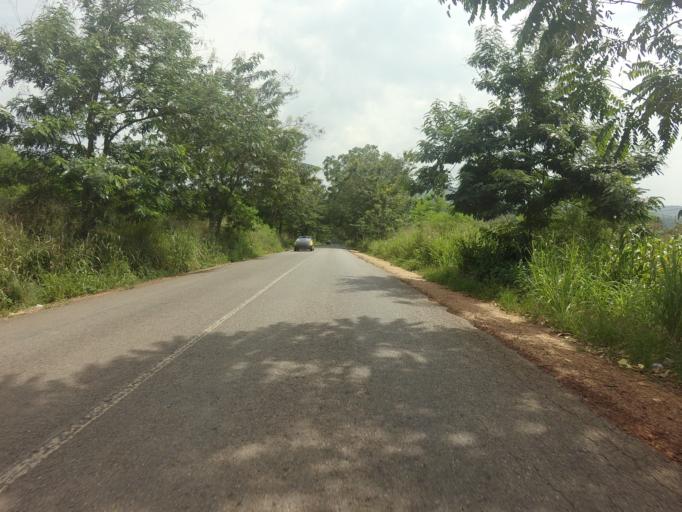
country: GH
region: Eastern
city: Aburi
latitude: 5.9558
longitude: -0.2151
